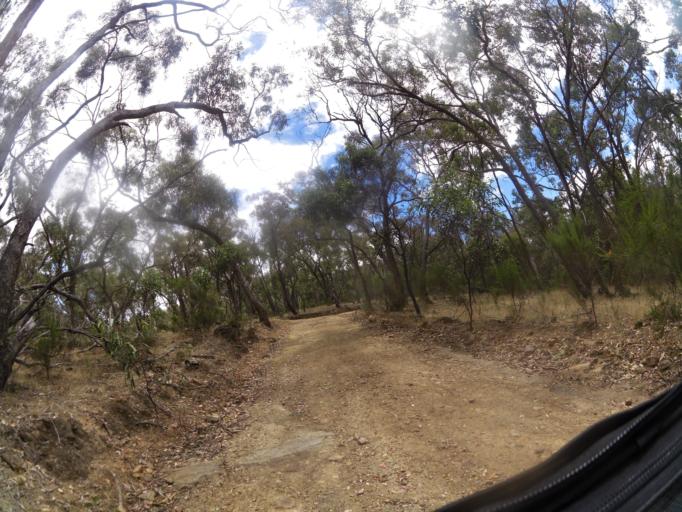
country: AU
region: Victoria
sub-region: Mount Alexander
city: Castlemaine
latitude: -37.0493
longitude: 144.2689
